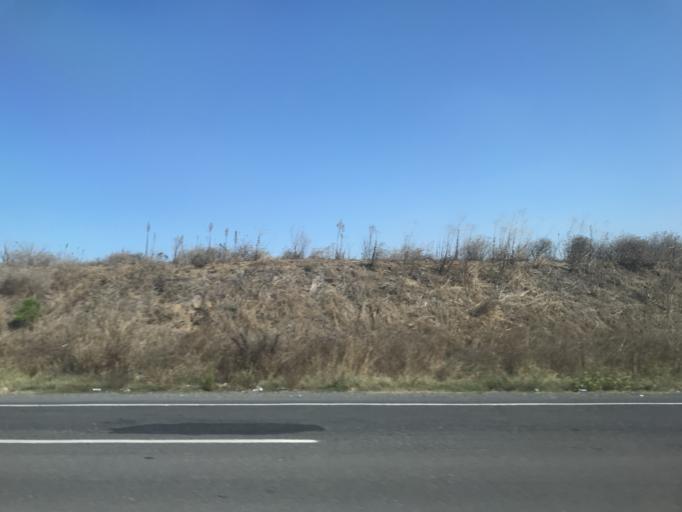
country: TR
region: Tekirdag
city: Muratli
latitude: 41.0922
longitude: 27.4921
